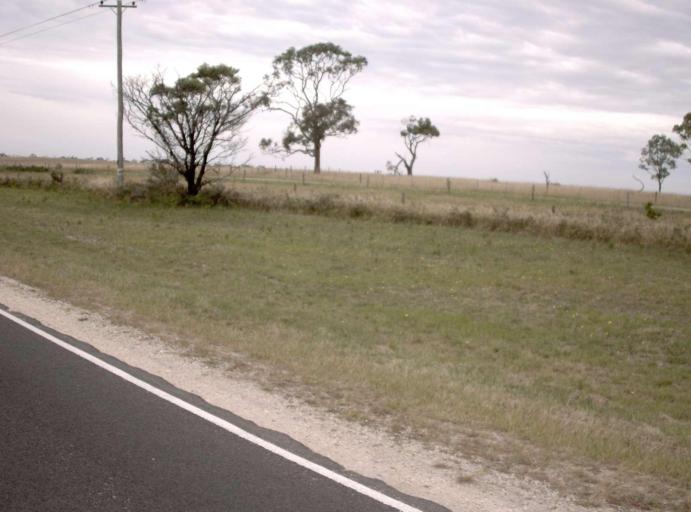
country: AU
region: Victoria
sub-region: Wellington
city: Sale
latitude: -38.1983
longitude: 147.3043
